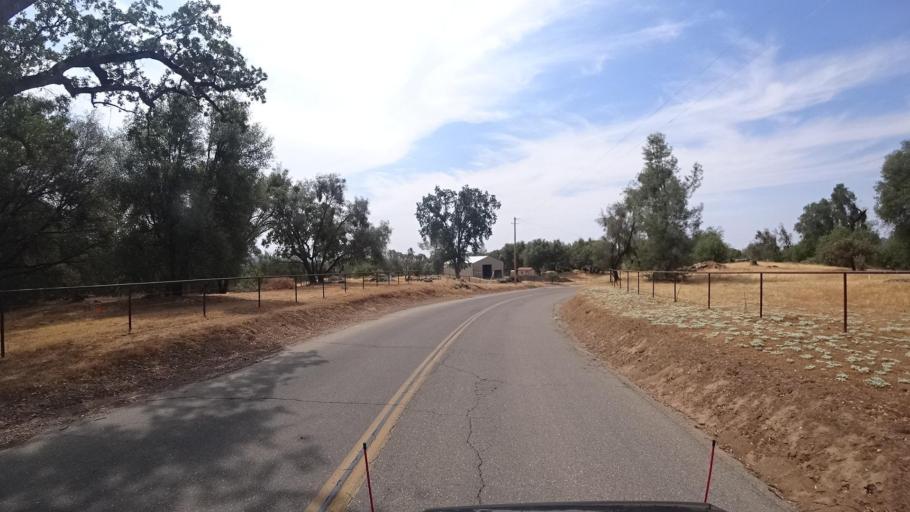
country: US
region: California
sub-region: Mariposa County
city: Midpines
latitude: 37.4931
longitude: -119.8893
